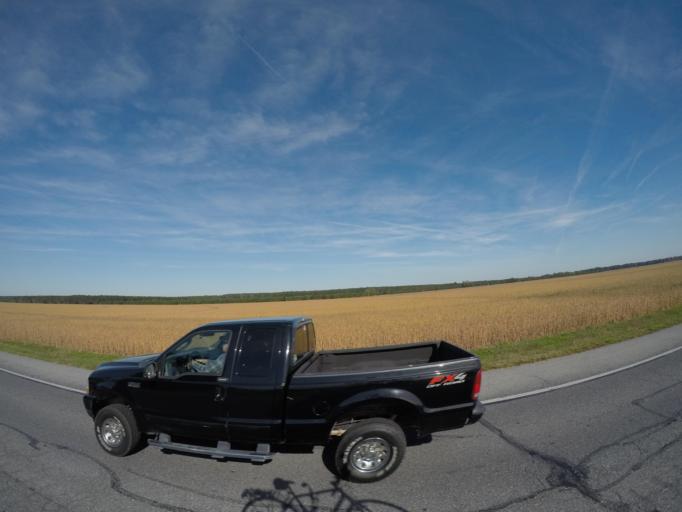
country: US
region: Delaware
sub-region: Sussex County
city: Milton
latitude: 38.7855
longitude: -75.3502
